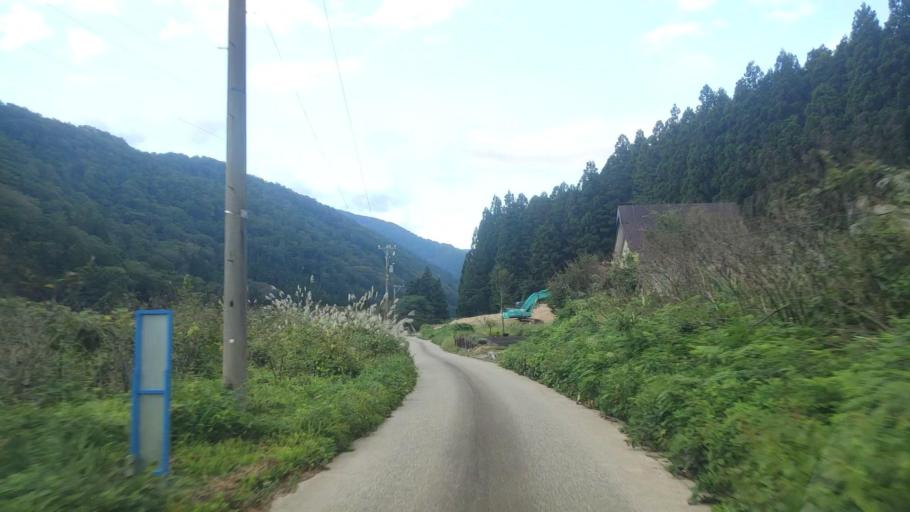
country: JP
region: Toyama
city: Yatsuomachi-higashikumisaka
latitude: 36.4249
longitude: 137.0826
